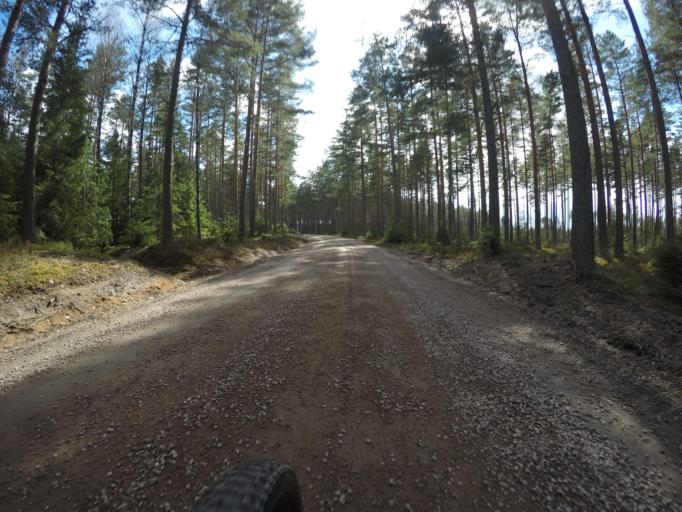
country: SE
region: Vaestmanland
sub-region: Kungsors Kommun
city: Kungsoer
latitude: 59.3721
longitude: 16.1006
